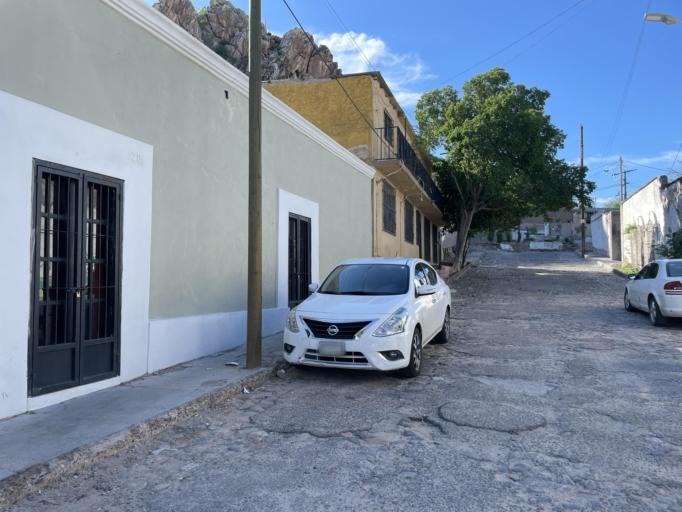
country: MX
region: Sonora
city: Hermosillo
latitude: 29.0757
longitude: -110.9539
